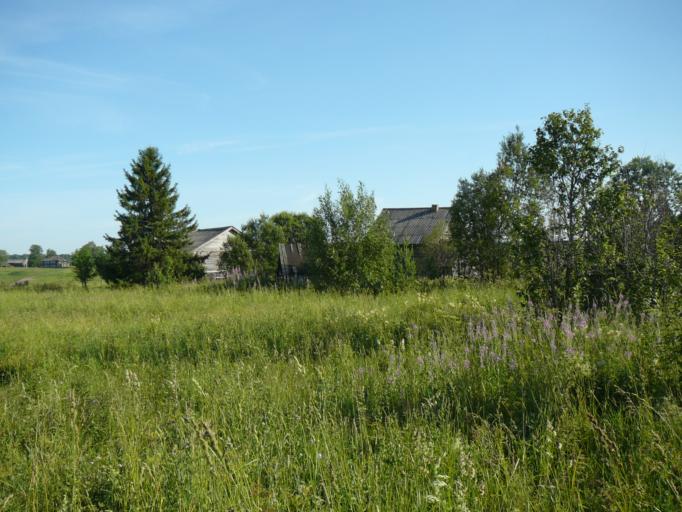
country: RU
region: Vologda
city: Ust'ye
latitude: 60.1474
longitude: 39.5610
